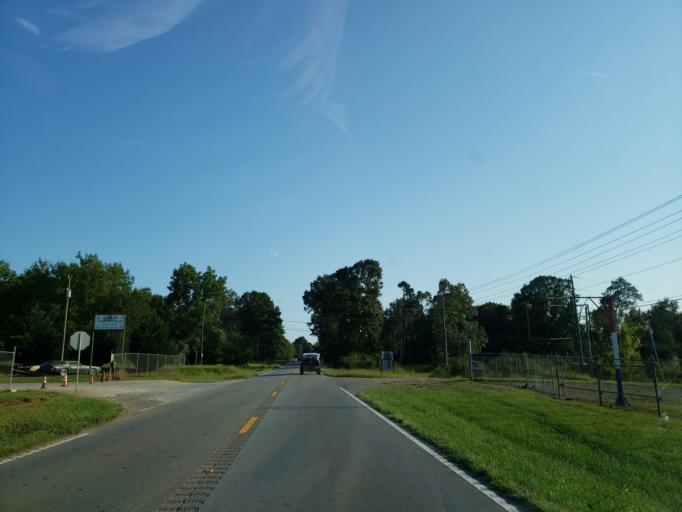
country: US
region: Georgia
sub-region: Murray County
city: Chatsworth
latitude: 34.7933
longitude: -84.8235
